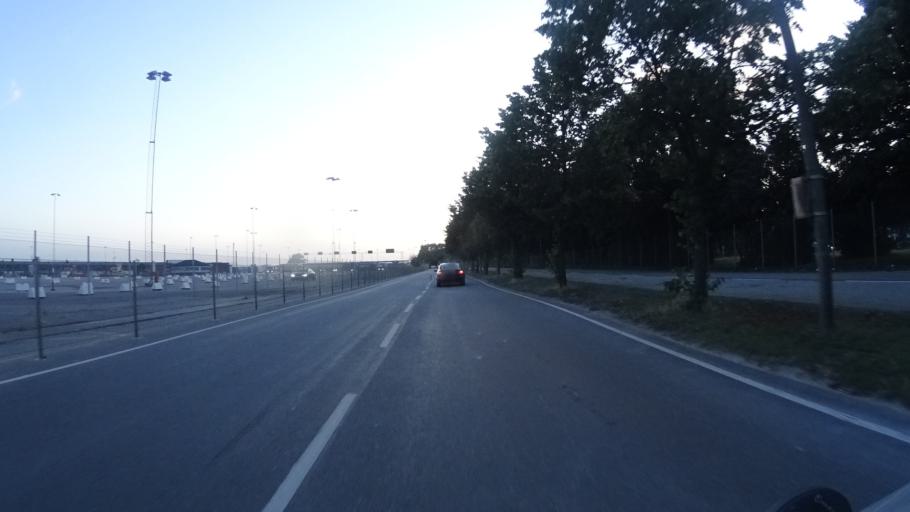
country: SE
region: Skane
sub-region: Trelleborgs Kommun
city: Trelleborg
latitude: 55.3733
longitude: 13.1476
